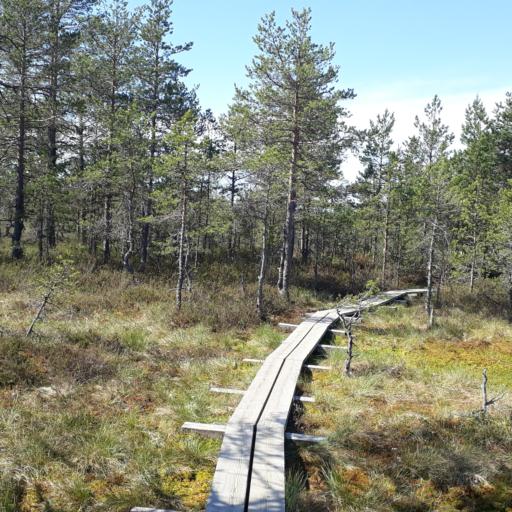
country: EE
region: Harju
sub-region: Loksa linn
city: Loksa
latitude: 59.4687
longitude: 25.6553
